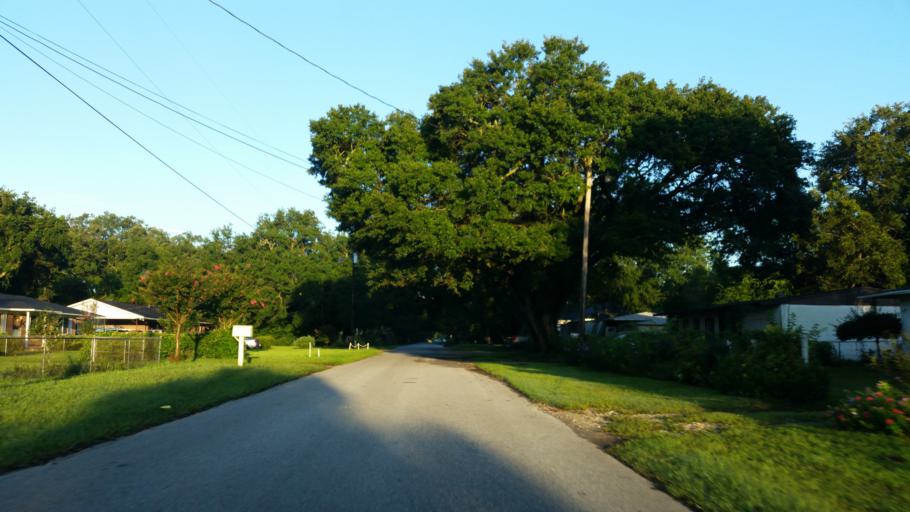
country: US
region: Florida
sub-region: Escambia County
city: Ferry Pass
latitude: 30.4982
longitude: -87.2149
